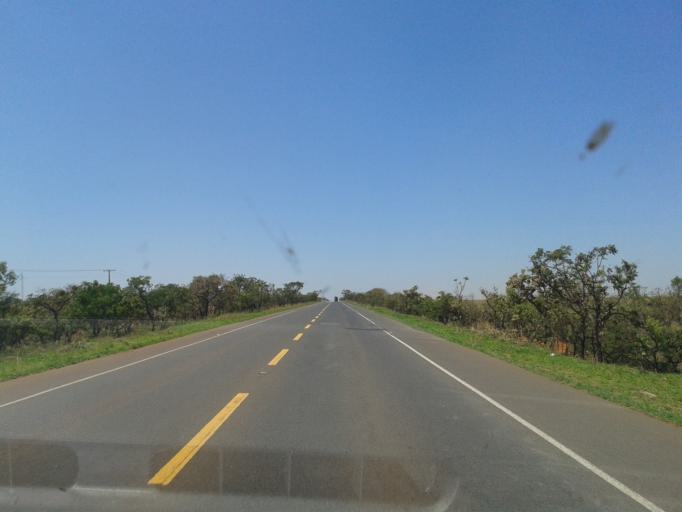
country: BR
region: Minas Gerais
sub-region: Patrocinio
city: Patrocinio
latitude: -19.2932
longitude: -47.4014
